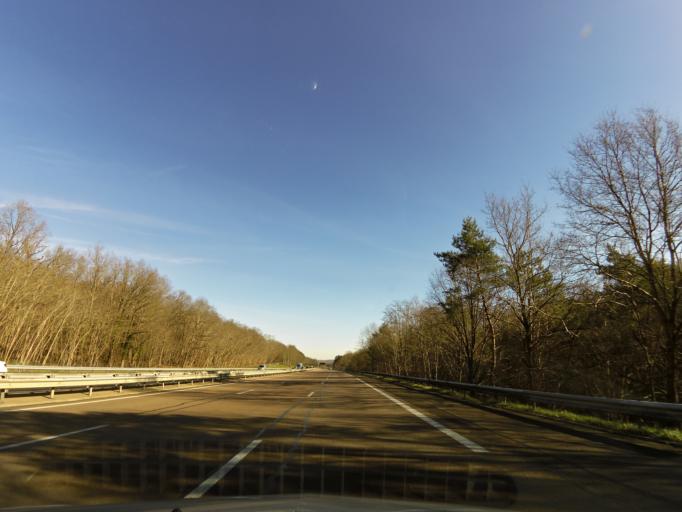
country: FR
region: Bourgogne
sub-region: Departement de l'Yonne
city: Appoigny
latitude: 47.8646
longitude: 3.5076
